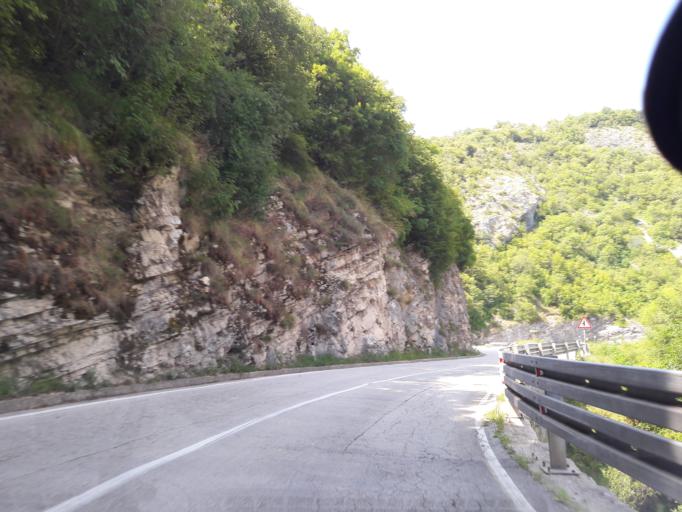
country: BA
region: Republika Srpska
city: Mrkonjic Grad
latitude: 44.4565
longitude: 17.1601
